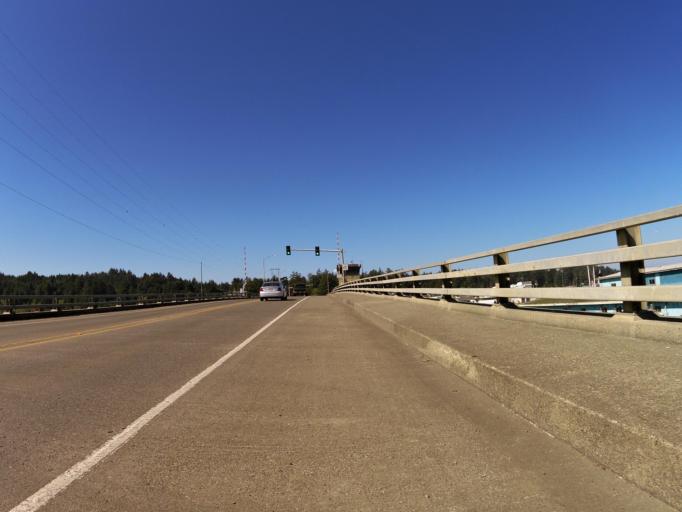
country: US
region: Oregon
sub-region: Coos County
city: Barview
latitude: 43.3386
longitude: -124.3197
